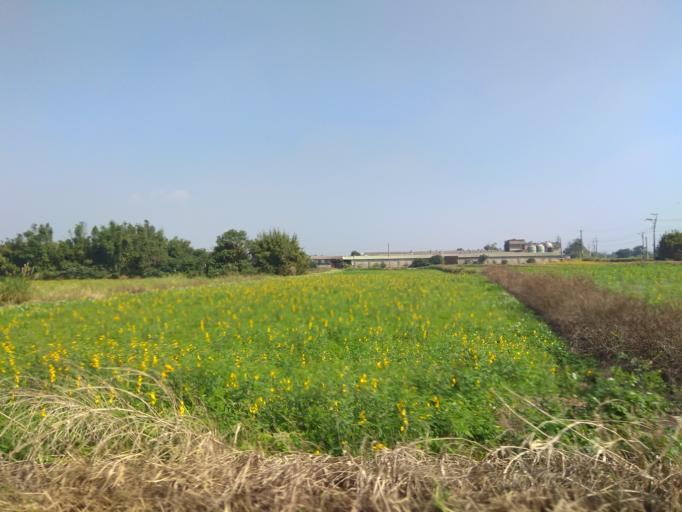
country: TW
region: Taiwan
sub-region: Hsinchu
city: Zhubei
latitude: 24.9876
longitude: 121.0756
